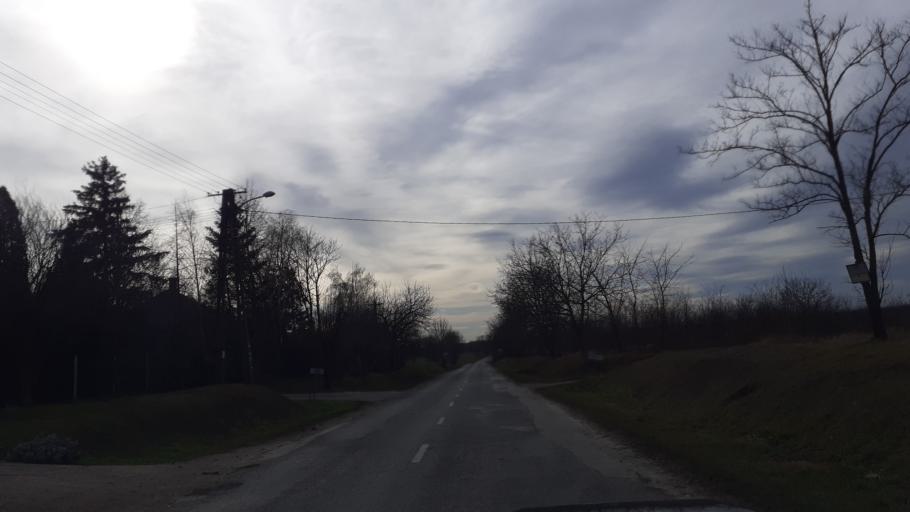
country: HU
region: Fejer
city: Sarbogard
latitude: 46.9264
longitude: 18.6810
